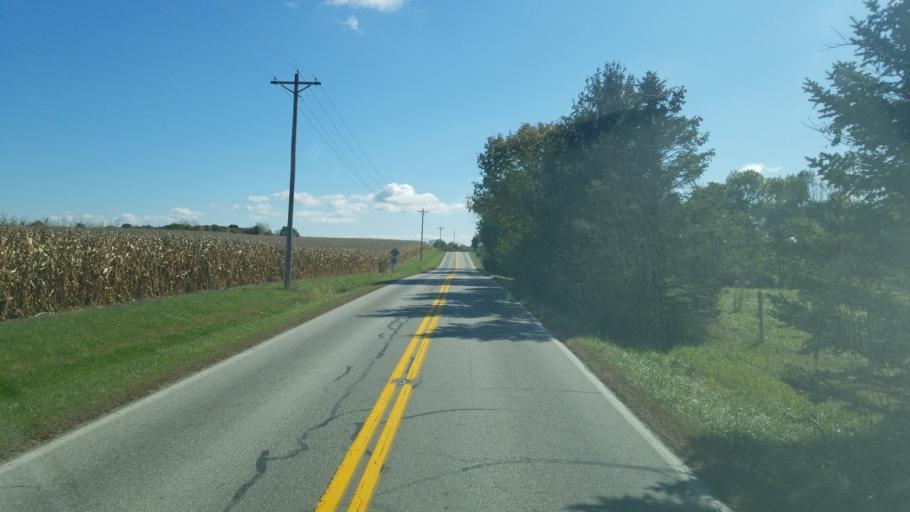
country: US
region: Ohio
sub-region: Highland County
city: Leesburg
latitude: 39.2789
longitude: -83.4933
